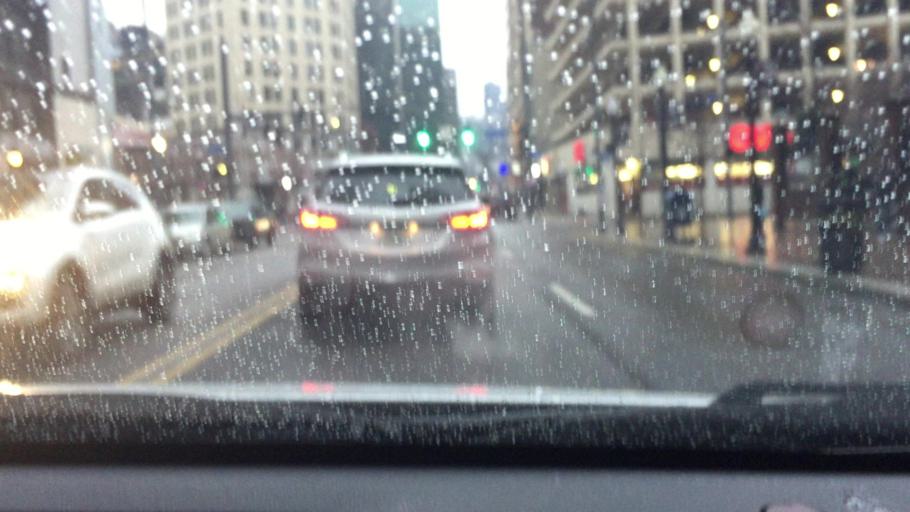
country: US
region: Pennsylvania
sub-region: Allegheny County
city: Pittsburgh
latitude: 40.4422
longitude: -80.0011
